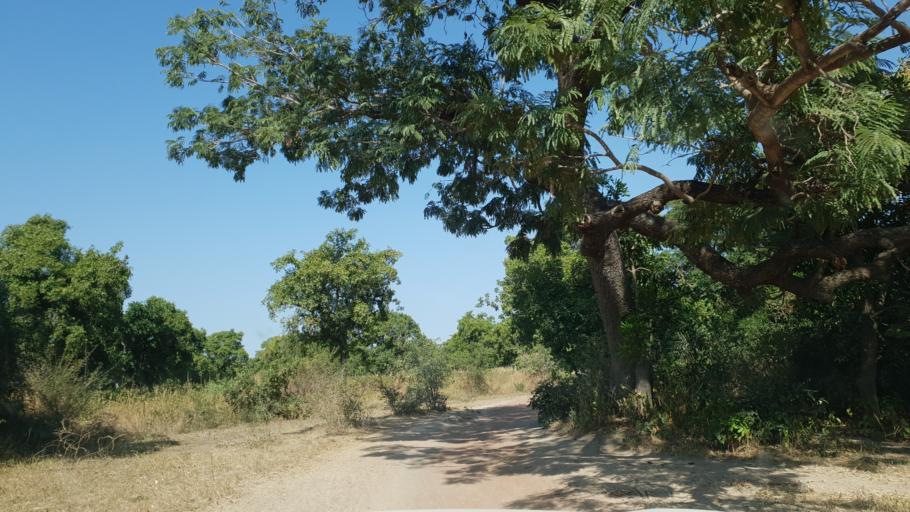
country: ML
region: Sikasso
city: Yorosso
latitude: 12.2689
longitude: -4.6980
